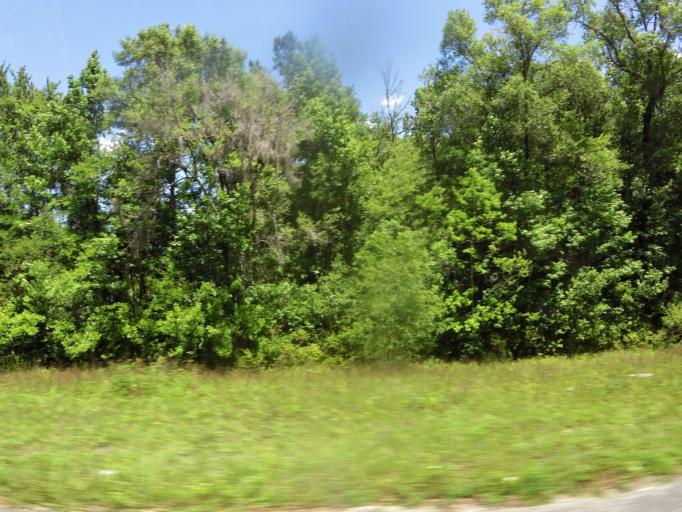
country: US
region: Florida
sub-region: Union County
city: Lake Butler
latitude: 30.0384
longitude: -82.2232
